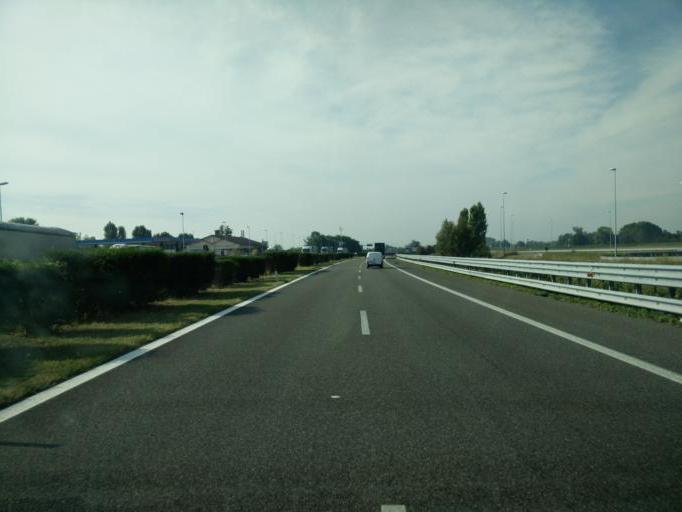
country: IT
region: Lombardy
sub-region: Provincia di Cremona
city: Battaglione-Bagnara
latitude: 45.1165
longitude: 10.0585
